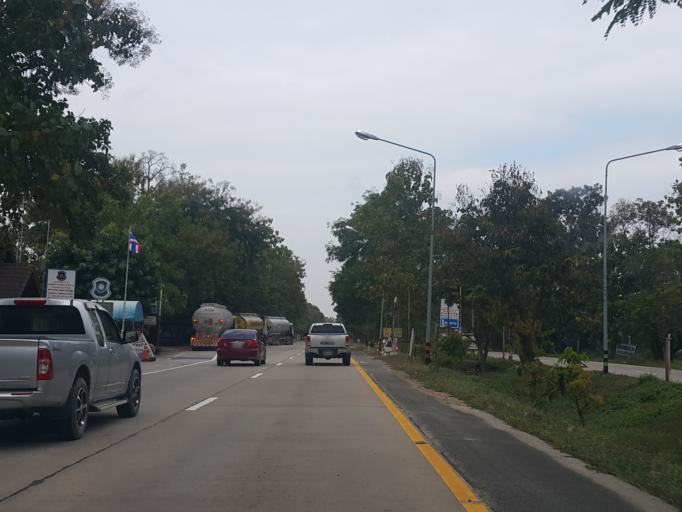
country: TH
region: Lamphun
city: Mae Tha
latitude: 18.5227
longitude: 99.0860
